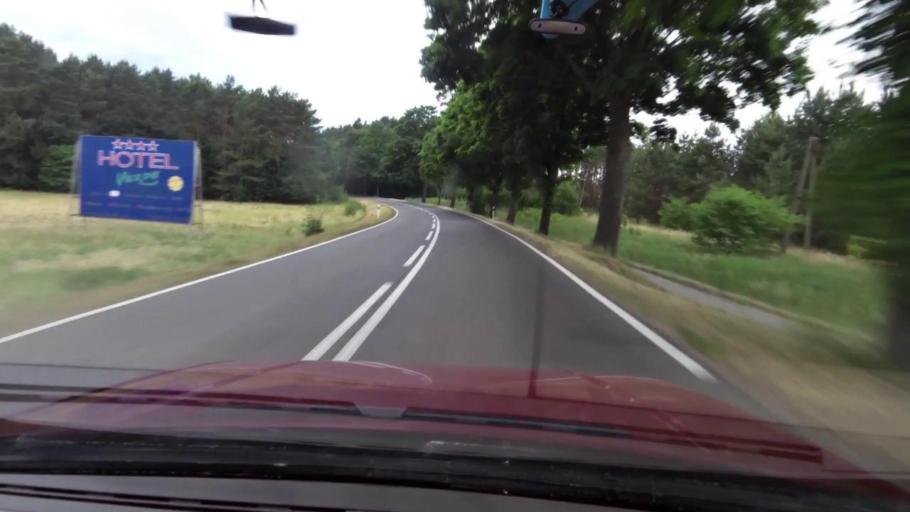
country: PL
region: West Pomeranian Voivodeship
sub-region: Powiat koszalinski
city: Sianow
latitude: 54.1843
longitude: 16.3156
